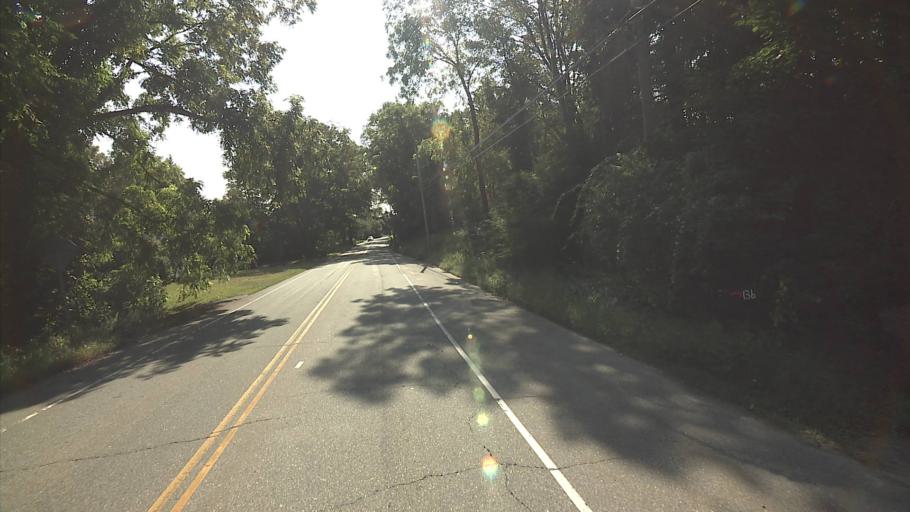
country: US
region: Connecticut
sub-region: New London County
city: Baltic
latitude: 41.5827
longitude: -72.1478
